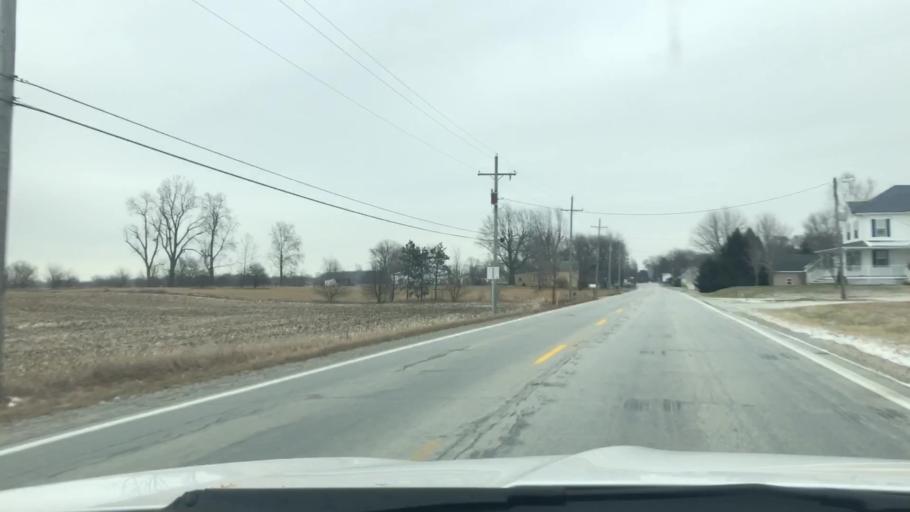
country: US
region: Indiana
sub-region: Fulton County
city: Rochester
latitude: 41.0543
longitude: -86.1316
